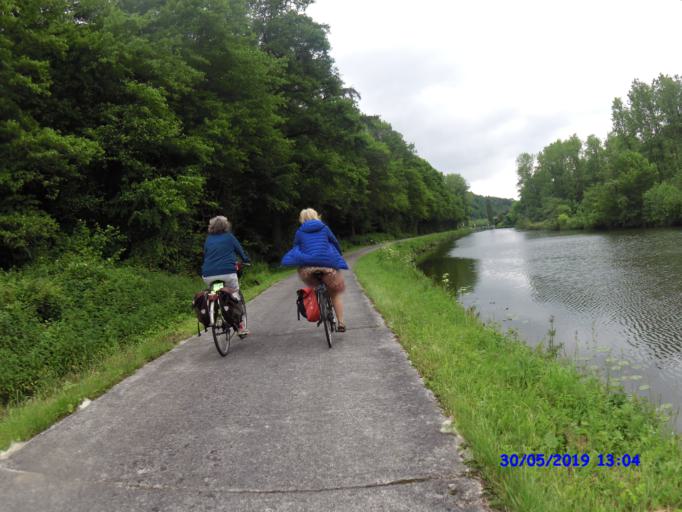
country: BE
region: Wallonia
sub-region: Province du Hainaut
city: Thuin
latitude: 50.3459
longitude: 4.3087
